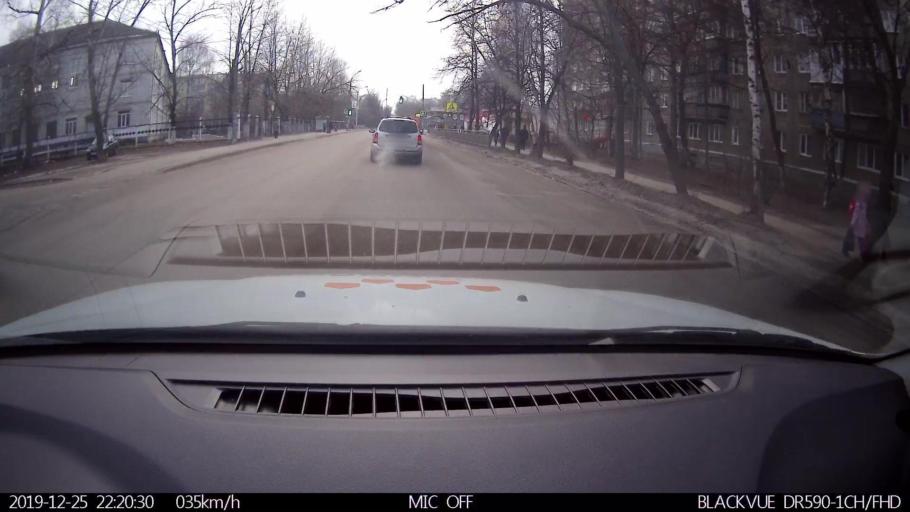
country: RU
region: Nizjnij Novgorod
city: Gorbatovka
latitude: 56.3366
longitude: 43.8398
